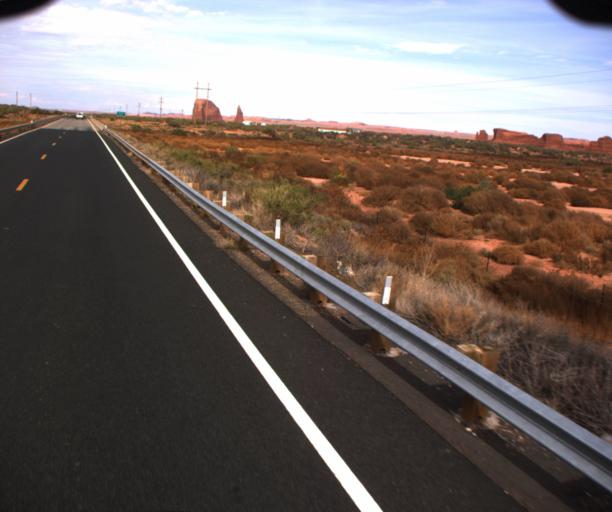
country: US
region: Arizona
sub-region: Apache County
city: Many Farms
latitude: 36.6256
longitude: -109.5833
